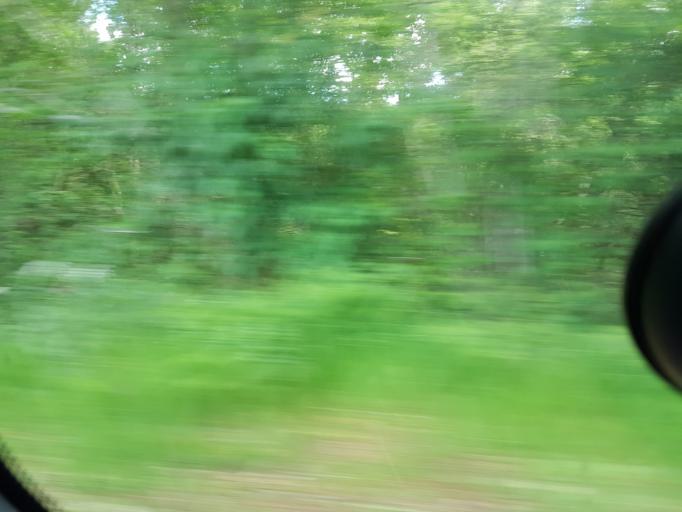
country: FR
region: Bourgogne
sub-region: Departement de la Cote-d'Or
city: Saulieu
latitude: 47.1788
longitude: 4.1039
